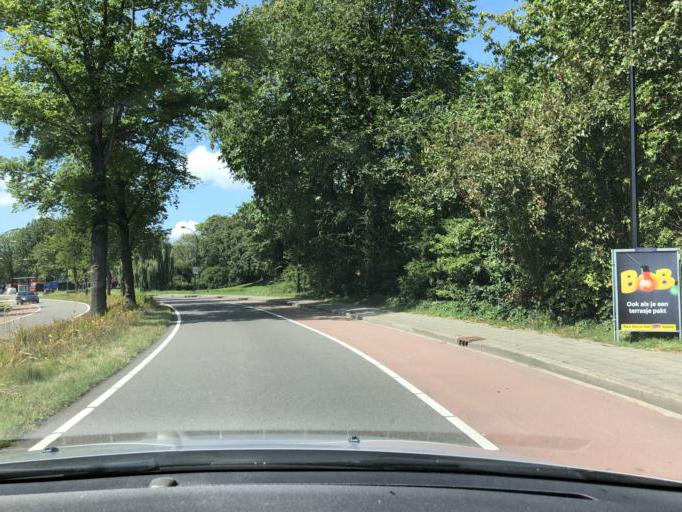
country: NL
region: North Holland
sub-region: Gemeente Edam-Volendam
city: Edam
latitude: 52.5097
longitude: 5.0478
